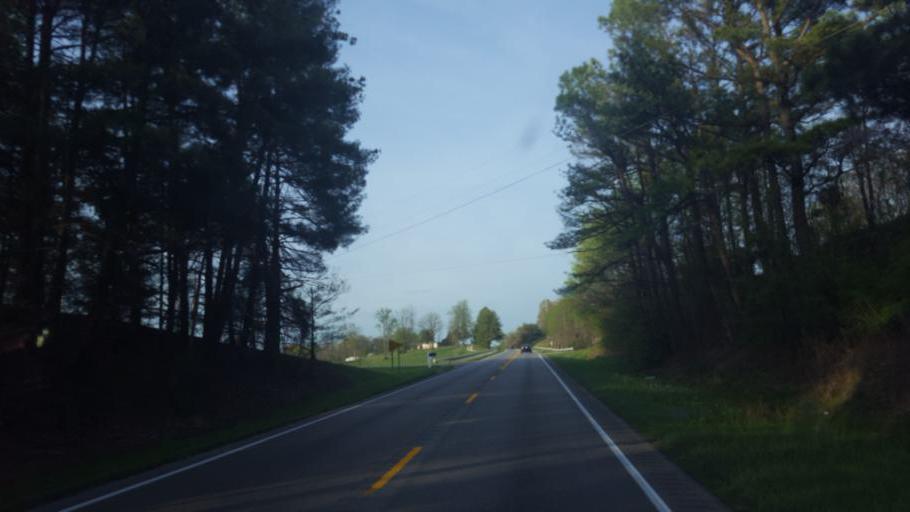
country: US
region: Kentucky
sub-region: Barren County
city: Glasgow
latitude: 36.9632
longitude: -85.9498
